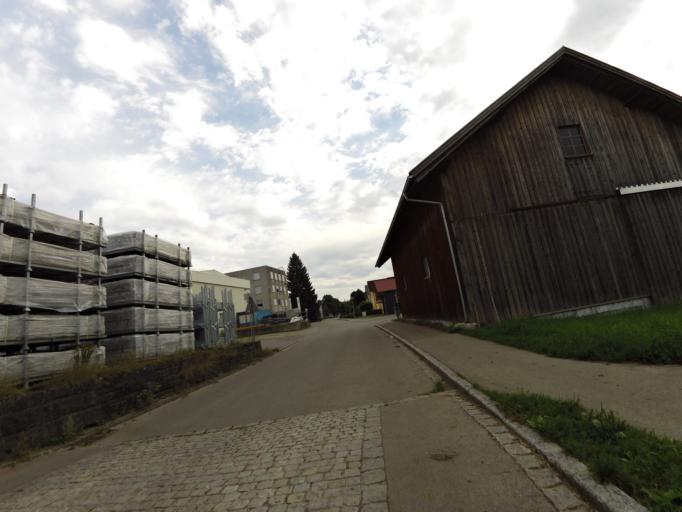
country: DE
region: Bavaria
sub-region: Swabia
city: Weiler-Simmerberg
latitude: 47.5866
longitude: 9.9185
